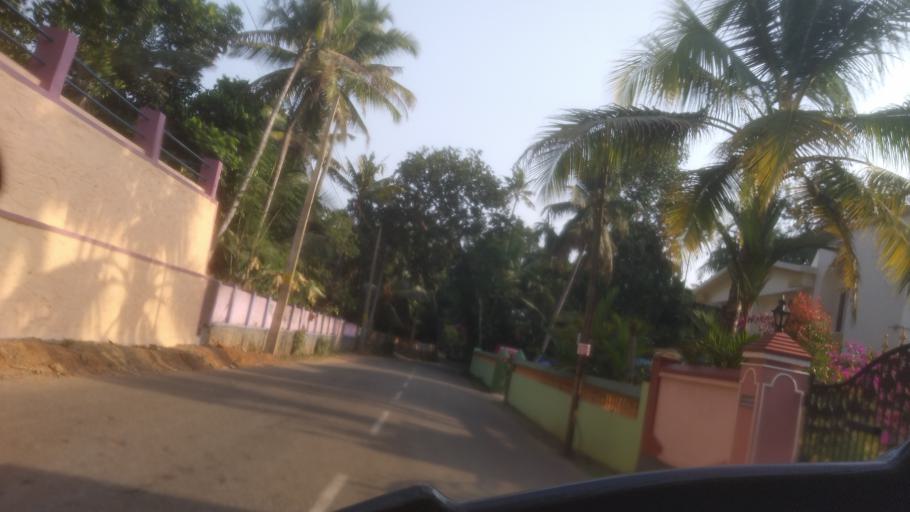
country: IN
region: Kerala
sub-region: Ernakulam
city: Piravam
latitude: 9.8215
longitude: 76.5022
